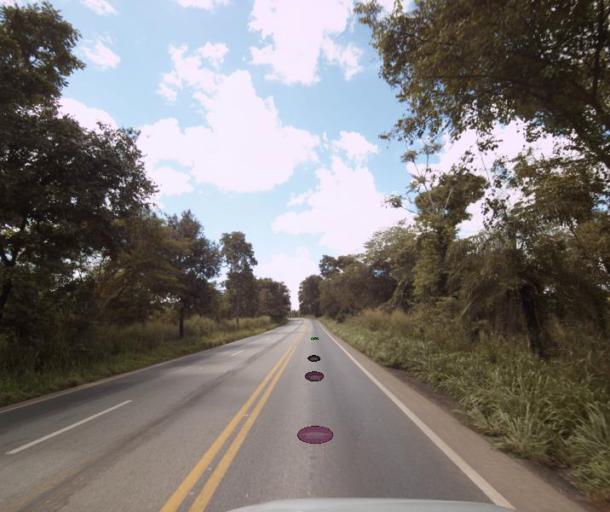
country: BR
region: Goias
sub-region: Porangatu
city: Porangatu
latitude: -13.7628
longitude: -49.0285
